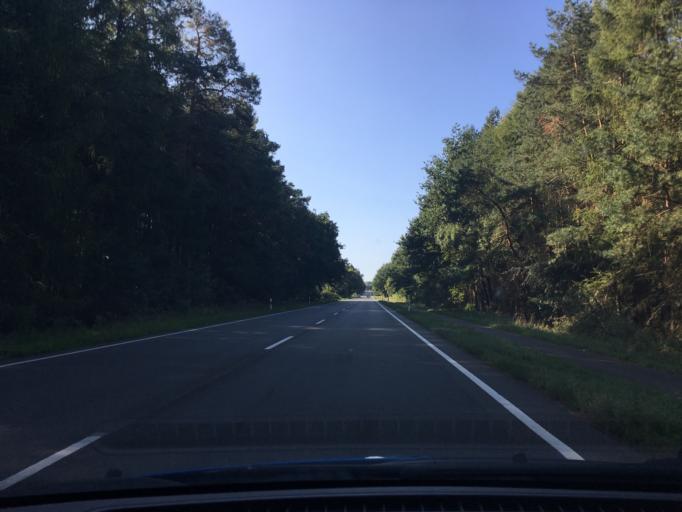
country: DE
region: Lower Saxony
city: Betzendorf
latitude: 53.1657
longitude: 10.3041
